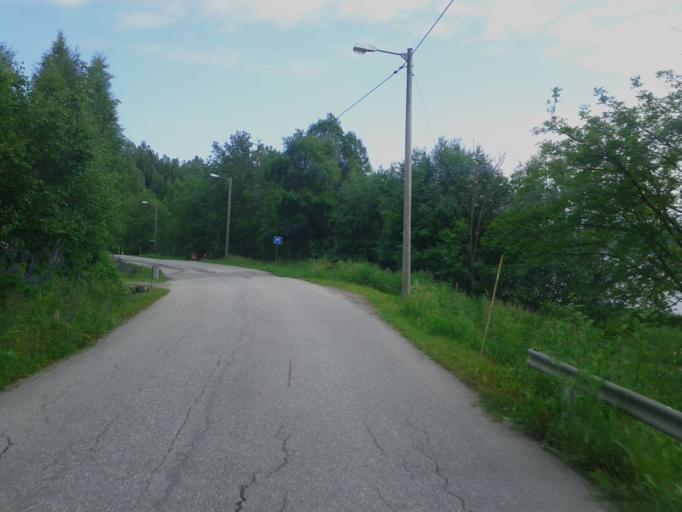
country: SE
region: Vaesternorrland
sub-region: OErnskoeldsviks Kommun
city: Ornskoldsvik
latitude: 63.2669
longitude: 18.8063
